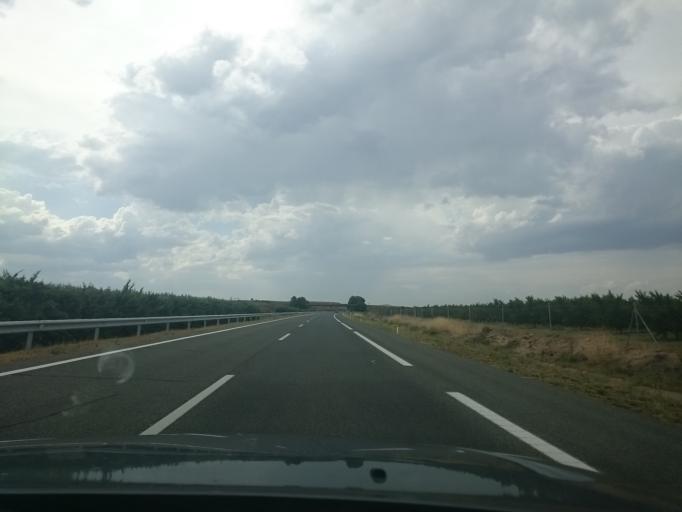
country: ES
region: Navarre
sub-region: Provincia de Navarra
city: Corella
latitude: 42.1544
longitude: -1.8086
